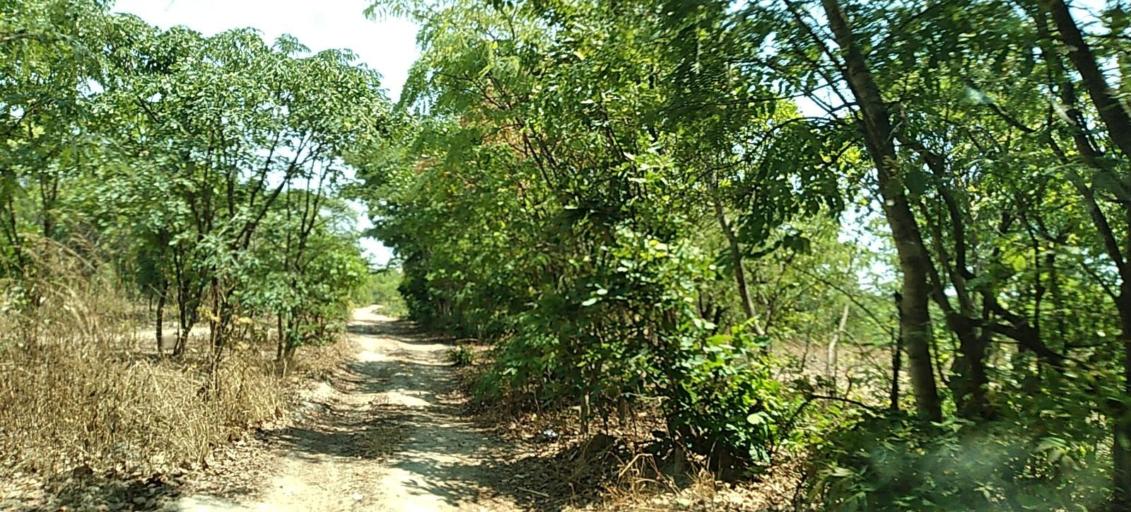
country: ZM
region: Copperbelt
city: Luanshya
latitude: -12.9924
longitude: 28.3279
